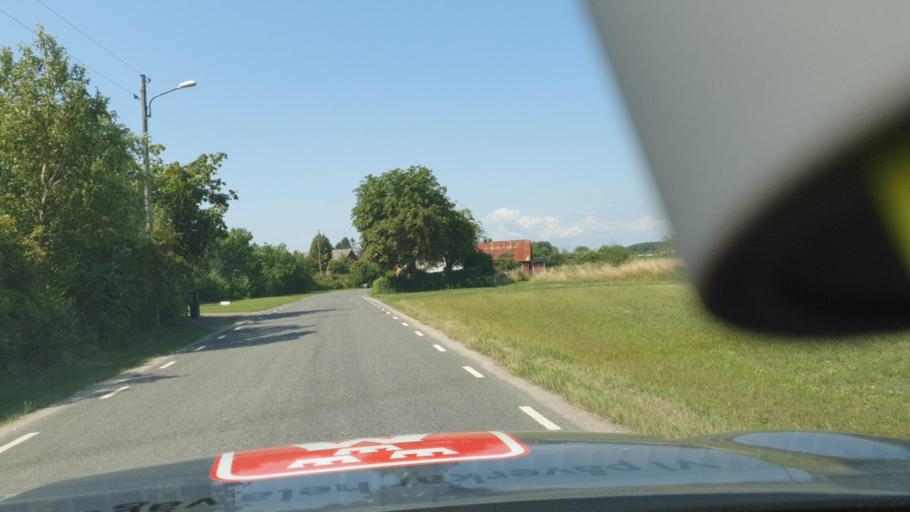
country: SE
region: Skane
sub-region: Kristianstads Kommun
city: Fjalkinge
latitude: 56.0578
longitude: 14.3721
